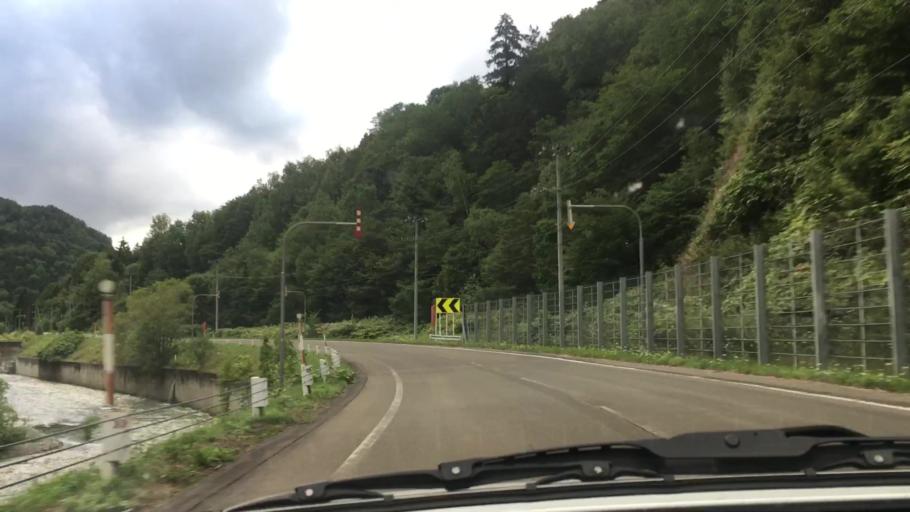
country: JP
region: Hokkaido
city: Shimo-furano
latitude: 43.0437
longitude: 142.5252
